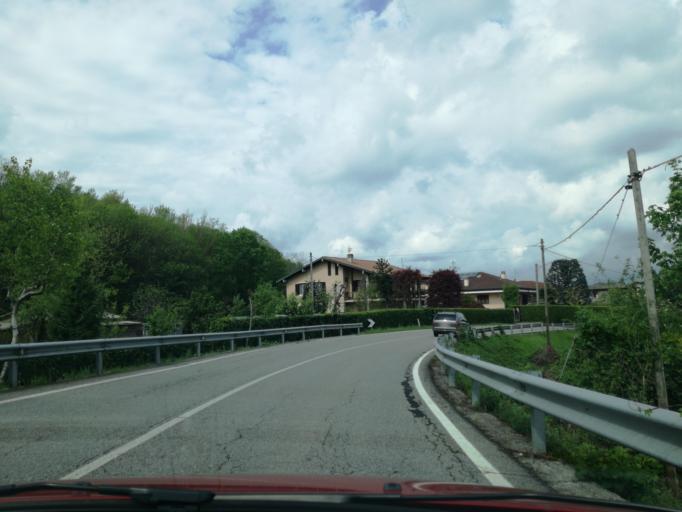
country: IT
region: Lombardy
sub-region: Provincia di Lecco
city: Barzago
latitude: 45.7581
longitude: 9.3222
